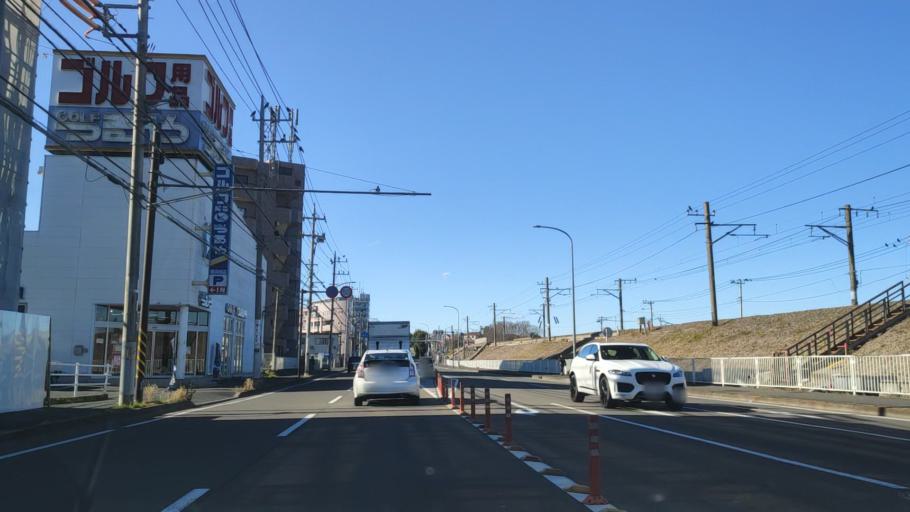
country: JP
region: Tokyo
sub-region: Machida-shi
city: Machida
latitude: 35.5190
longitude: 139.5307
